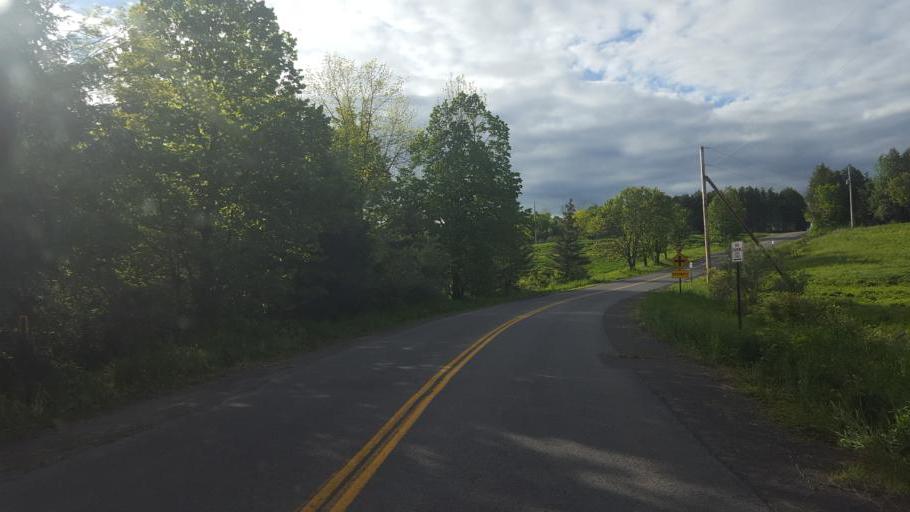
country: US
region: New York
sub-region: Otsego County
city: Richfield Springs
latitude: 42.9294
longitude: -74.9362
